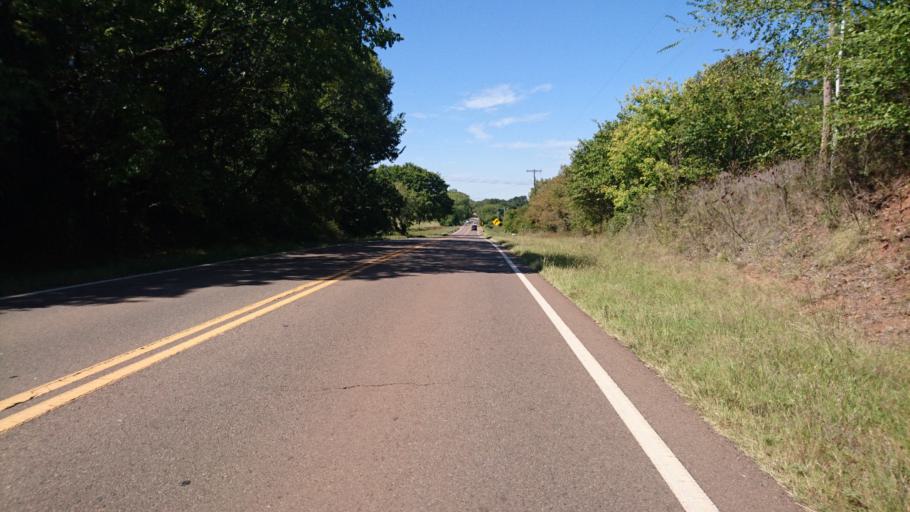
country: US
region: Oklahoma
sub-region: Oklahoma County
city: Luther
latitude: 35.6598
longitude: -97.2851
